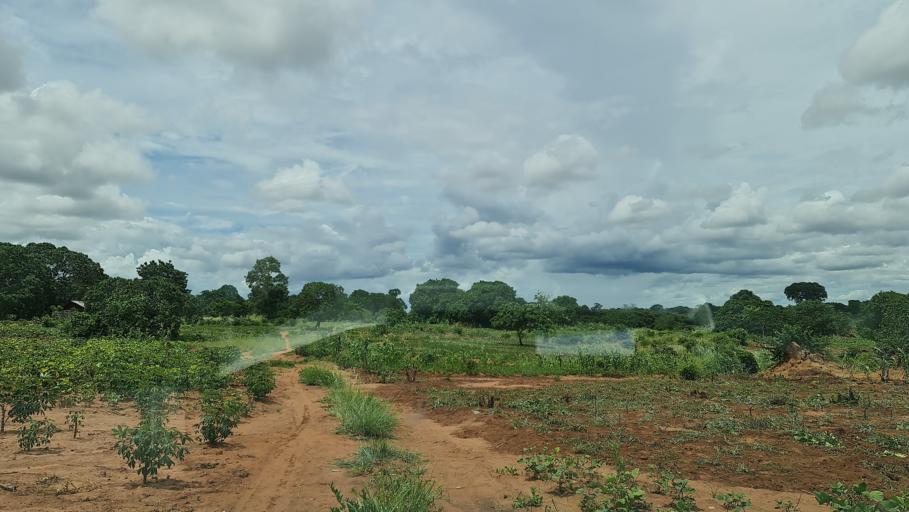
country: MZ
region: Nampula
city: Nacala
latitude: -14.7827
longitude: 39.9819
